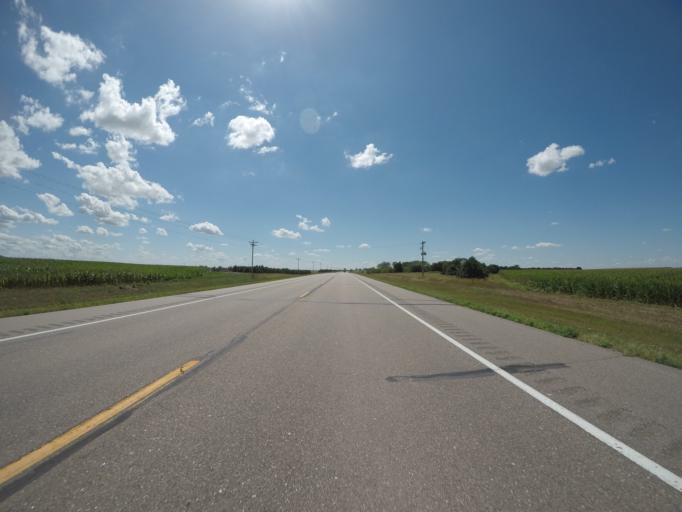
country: US
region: Nebraska
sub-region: Chase County
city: Imperial
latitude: 40.4947
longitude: -101.5678
